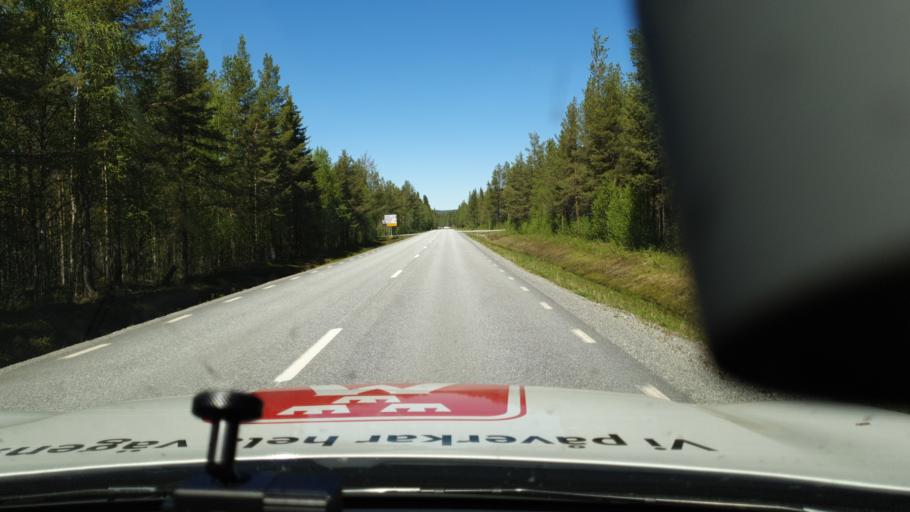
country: SE
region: Vaesterbotten
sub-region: Storumans Kommun
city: Storuman
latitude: 65.2059
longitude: 16.9936
